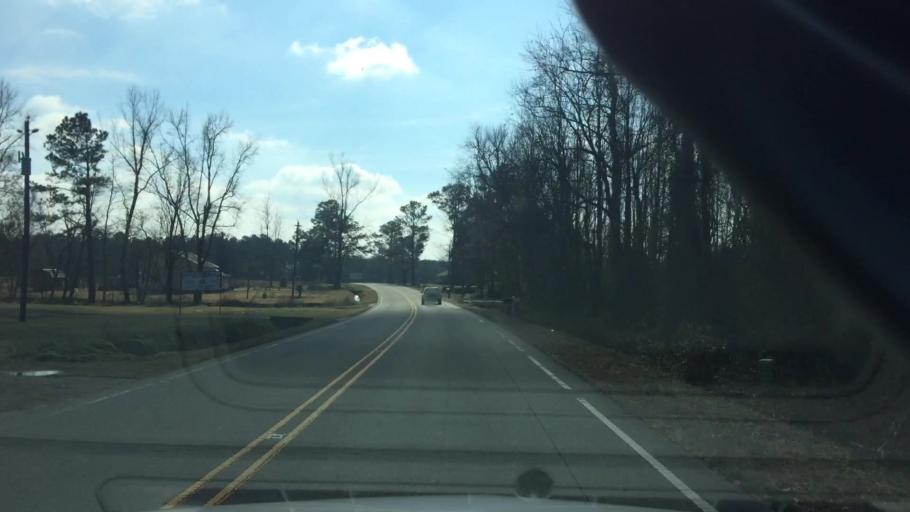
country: US
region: North Carolina
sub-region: Duplin County
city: Beulaville
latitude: 34.8561
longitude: -77.7977
